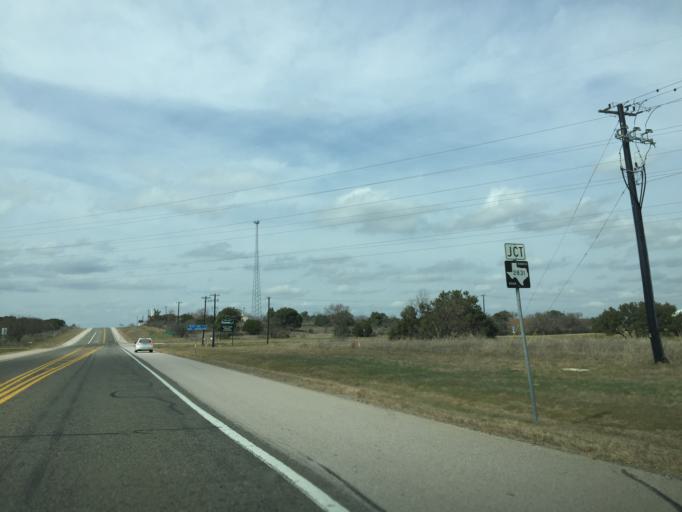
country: US
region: Texas
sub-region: Burnet County
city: Granite Shoals
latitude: 30.5272
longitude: -98.4222
